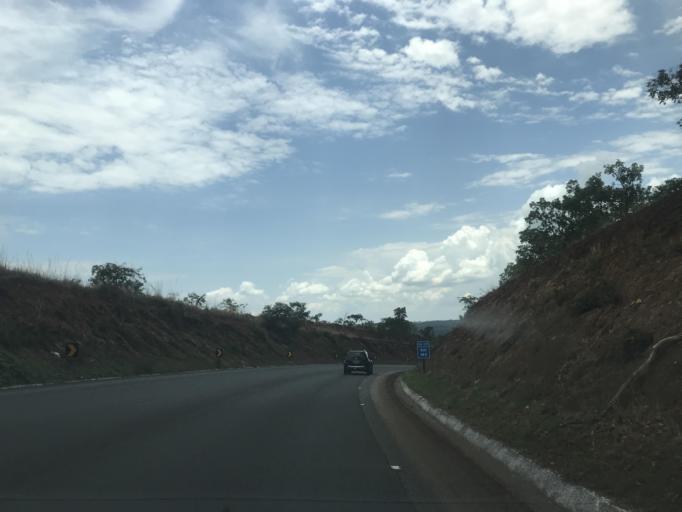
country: BR
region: Goias
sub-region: Vianopolis
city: Vianopolis
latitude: -16.9424
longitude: -48.5571
